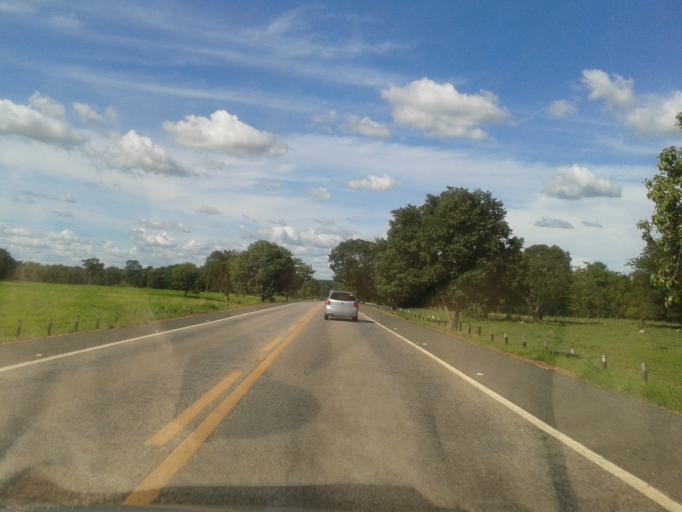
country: BR
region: Goias
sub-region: Mozarlandia
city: Mozarlandia
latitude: -15.0074
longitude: -50.5918
